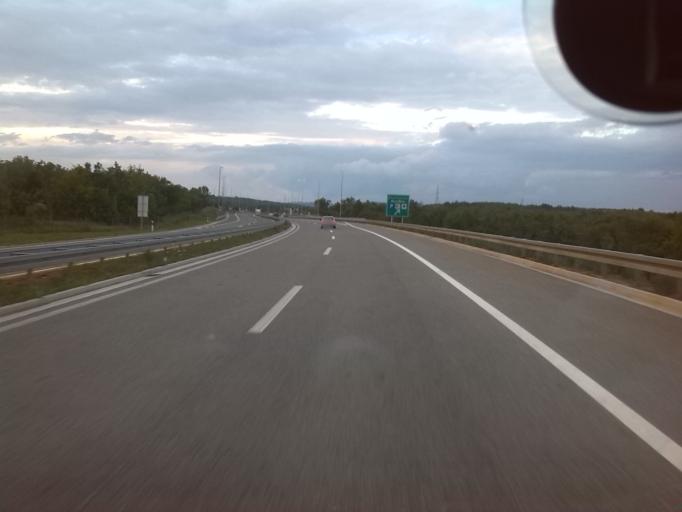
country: HR
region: Istarska
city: Buje
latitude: 45.4350
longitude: 13.6158
